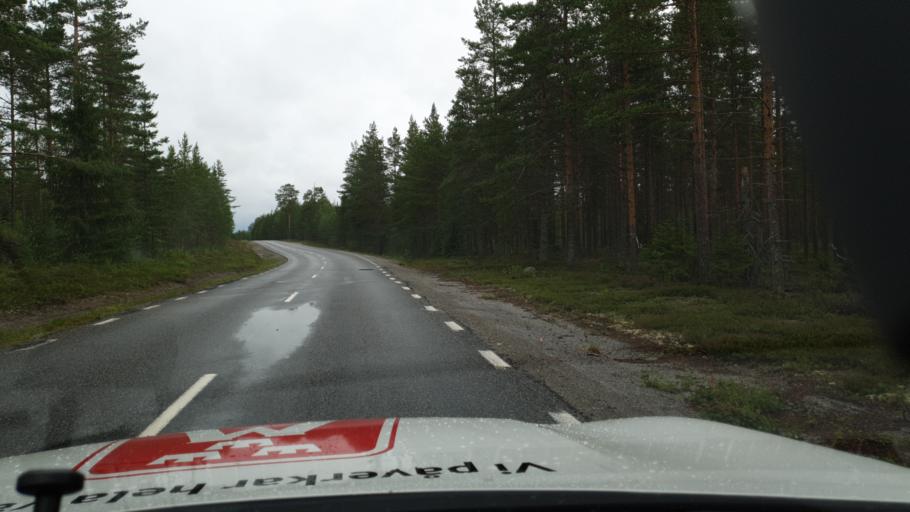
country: SE
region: Vaesterbotten
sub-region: Umea Kommun
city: Saevar
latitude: 63.9277
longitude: 20.5349
